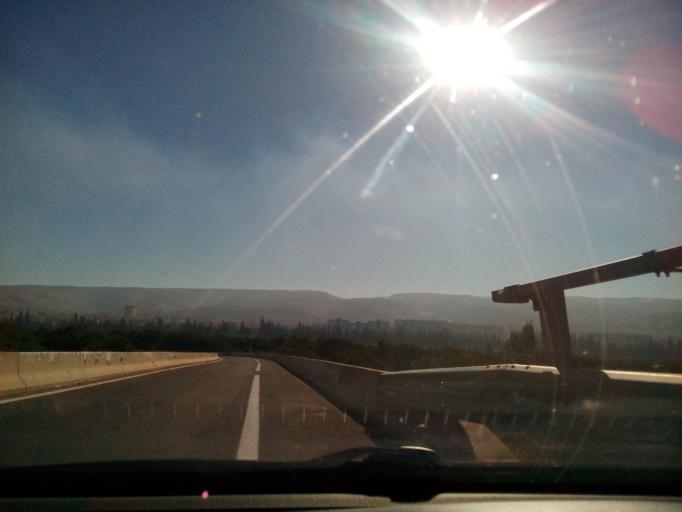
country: DZ
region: Relizane
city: Oued Rhiou
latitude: 35.9680
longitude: 0.8991
